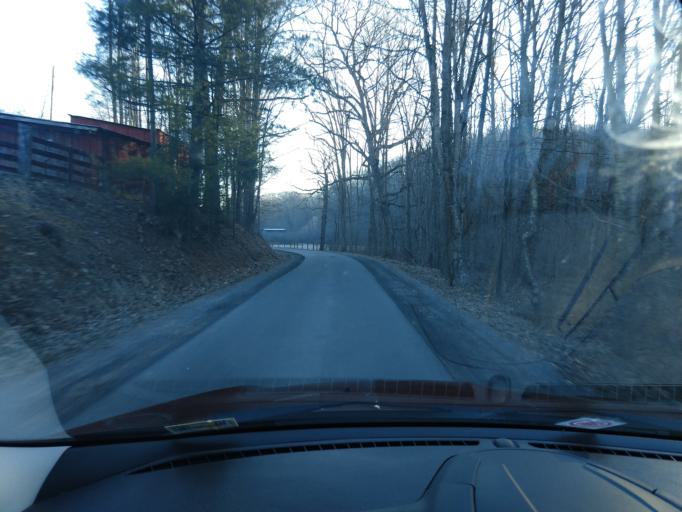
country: US
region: West Virginia
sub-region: Greenbrier County
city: Rainelle
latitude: 37.8747
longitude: -80.7264
